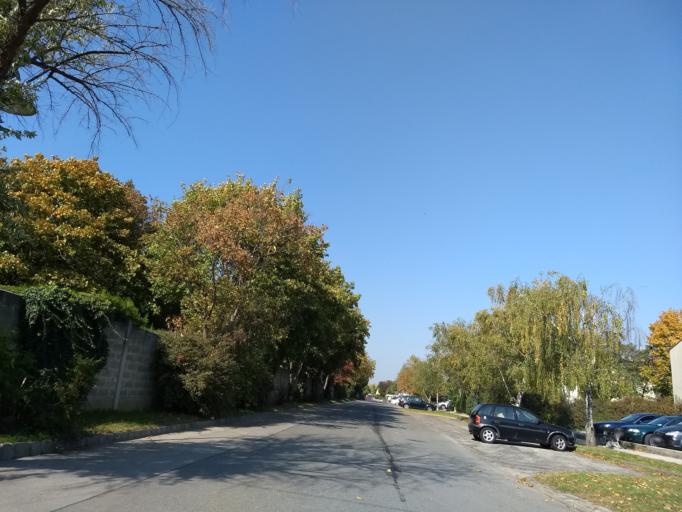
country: AT
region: Lower Austria
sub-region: Politischer Bezirk Modling
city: Perchtoldsdorf
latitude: 48.1168
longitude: 16.2777
